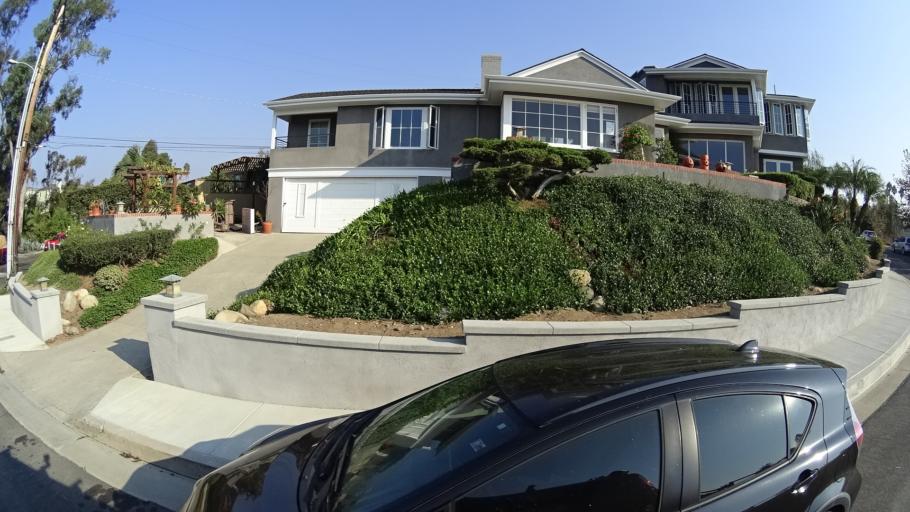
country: US
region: California
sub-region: Orange County
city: San Clemente
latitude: 33.4110
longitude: -117.6077
